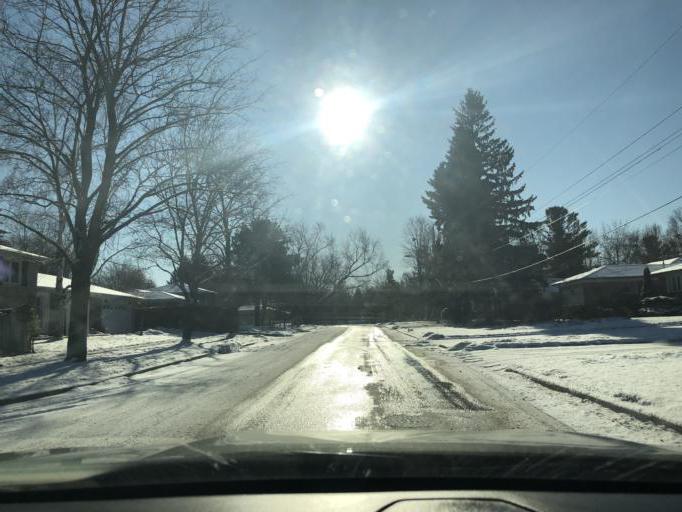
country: CA
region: Ontario
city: Scarborough
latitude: 43.7752
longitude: -79.1457
